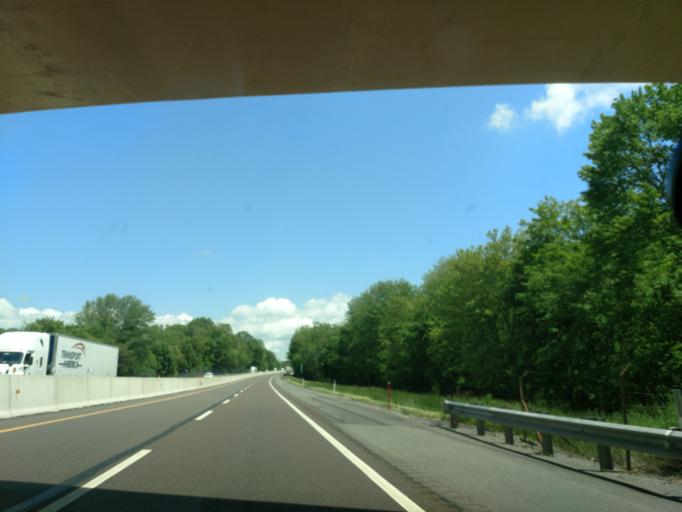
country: US
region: Pennsylvania
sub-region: Lancaster County
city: Clay
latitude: 40.2411
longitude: -76.2495
